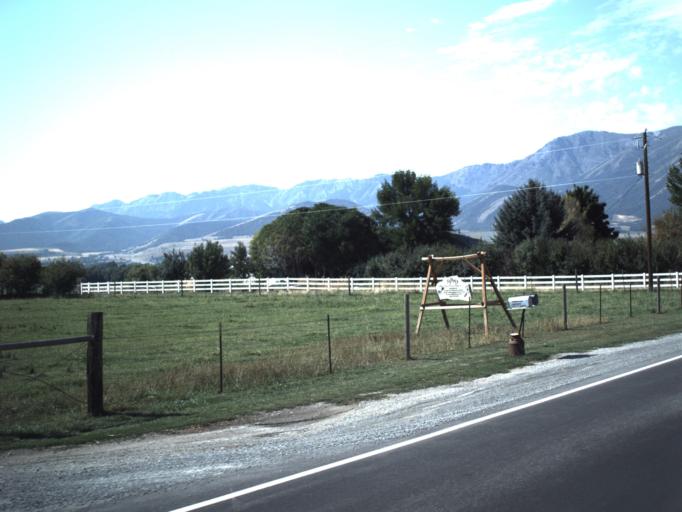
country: US
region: Utah
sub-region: Cache County
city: Wellsville
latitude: 41.6413
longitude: -111.9003
